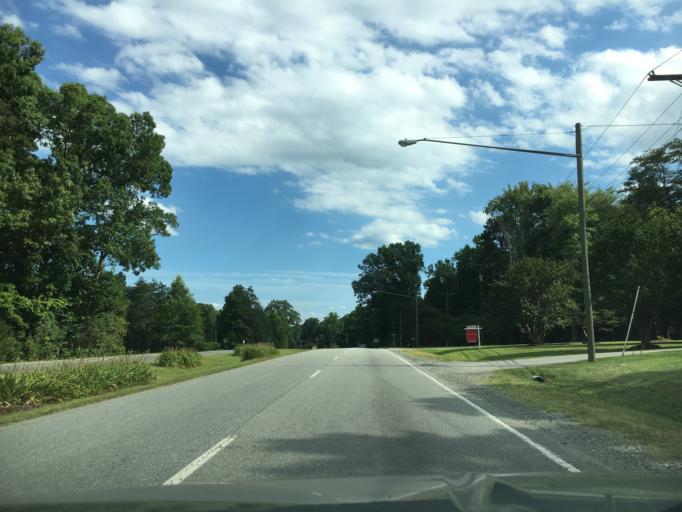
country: US
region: Virginia
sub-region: Halifax County
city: South Boston
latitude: 36.7221
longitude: -78.9183
